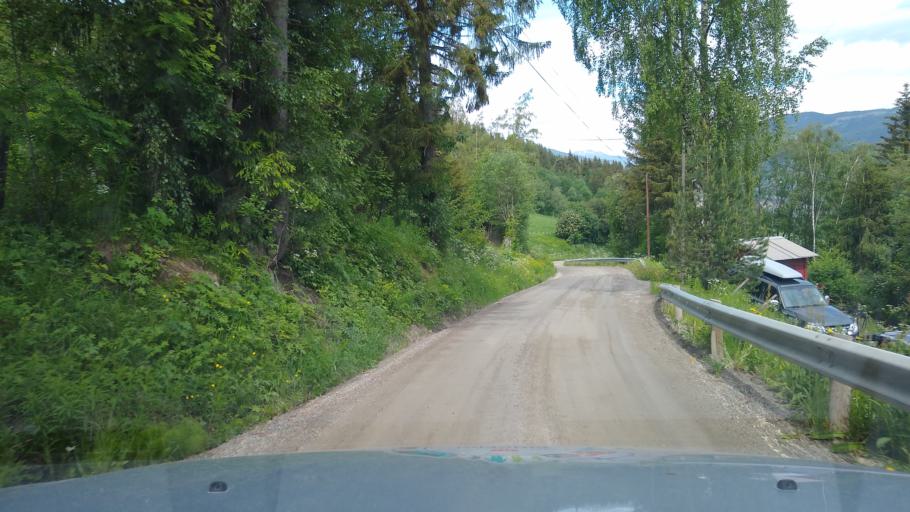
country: NO
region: Oppland
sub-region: Ringebu
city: Ringebu
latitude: 61.5107
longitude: 10.1355
